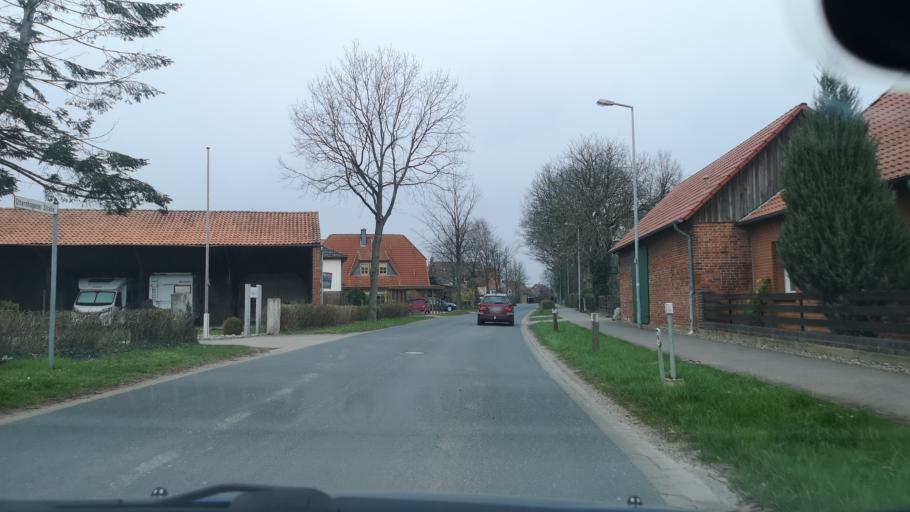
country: DE
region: Lower Saxony
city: Neustadt am Rubenberge
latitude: 52.5070
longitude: 9.5251
